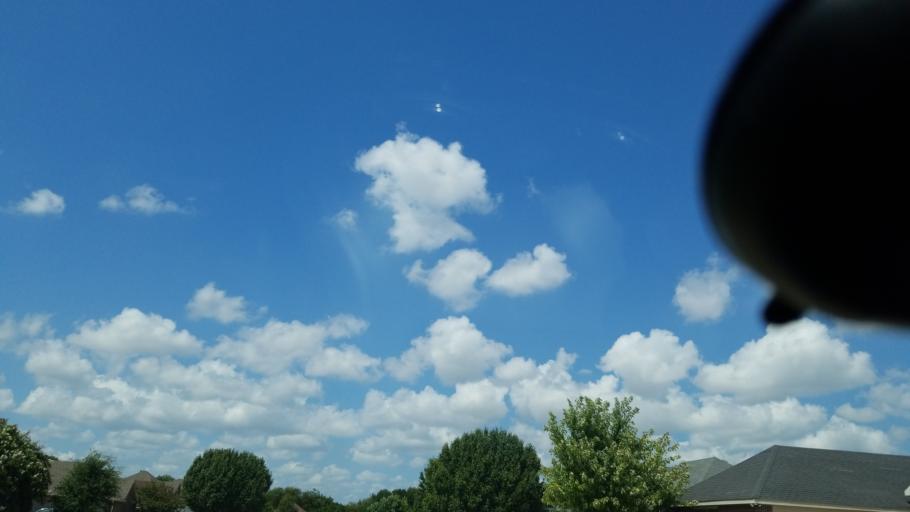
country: US
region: Texas
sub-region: Dallas County
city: Grand Prairie
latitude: 32.7233
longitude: -96.9894
